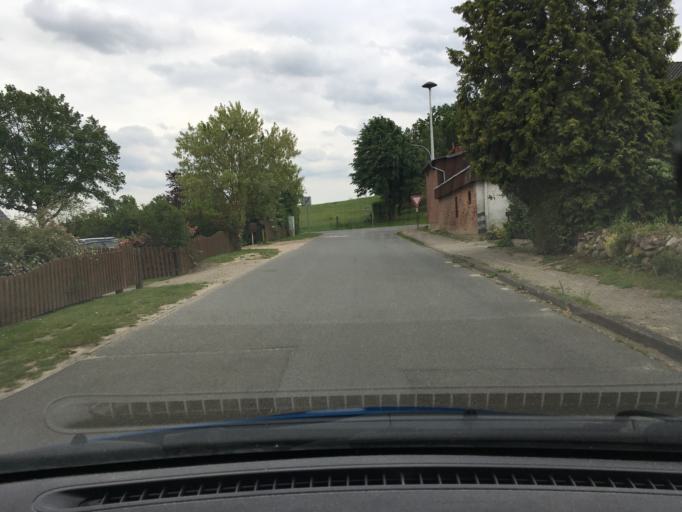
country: DE
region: Lower Saxony
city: Eyendorf
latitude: 53.2027
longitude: 10.1621
